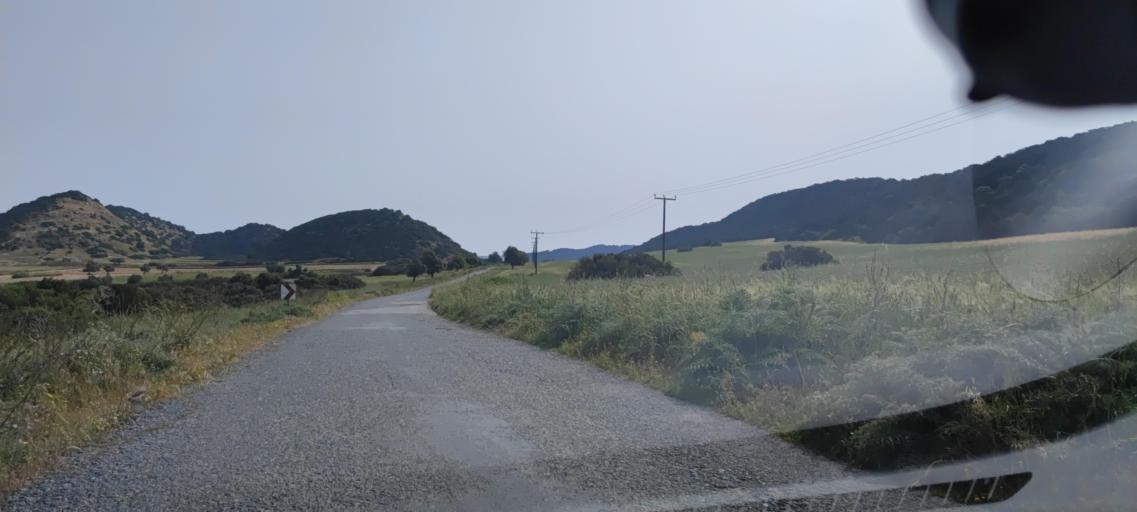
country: CY
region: Ammochostos
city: Rizokarpaso
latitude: 35.6317
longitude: 34.4974
